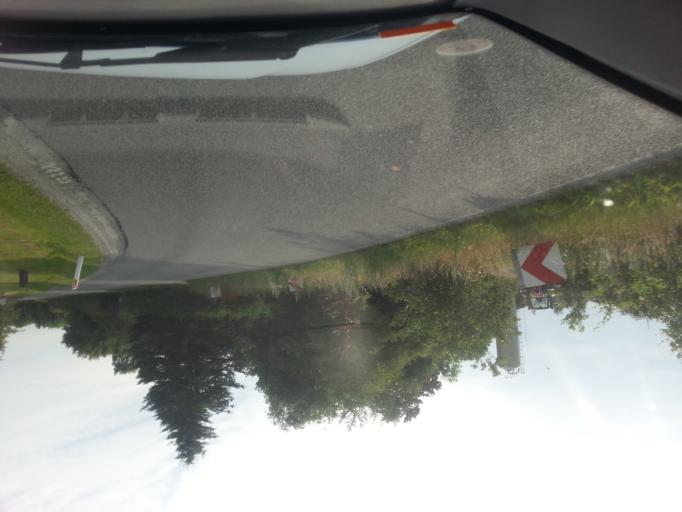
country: DK
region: South Denmark
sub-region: Vejen Kommune
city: Holsted
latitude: 55.4964
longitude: 8.9220
